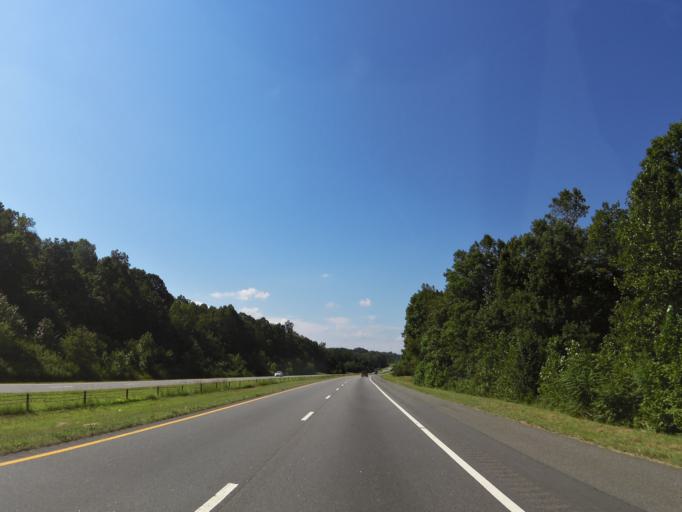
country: US
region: North Carolina
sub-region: Catawba County
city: Mountain View
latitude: 35.6623
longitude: -81.3238
